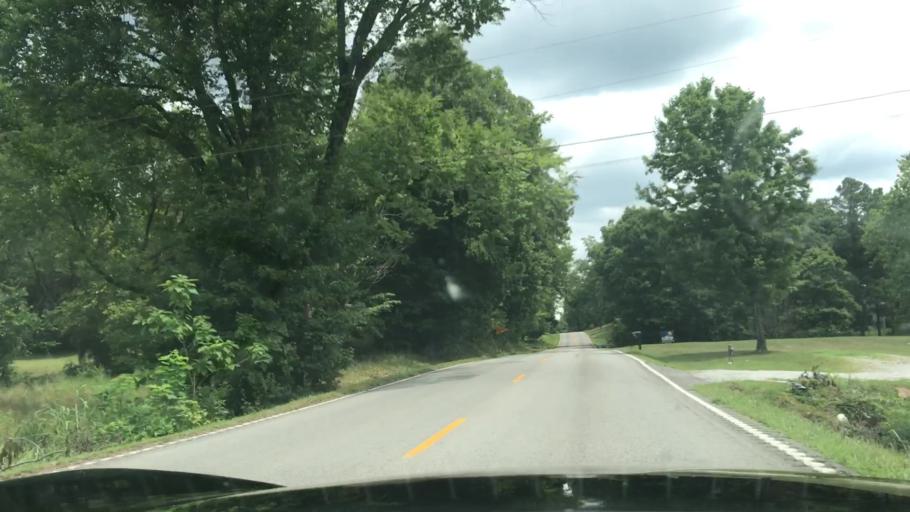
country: US
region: Kentucky
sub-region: Muhlenberg County
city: Greenville
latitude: 37.2033
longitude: -87.0869
